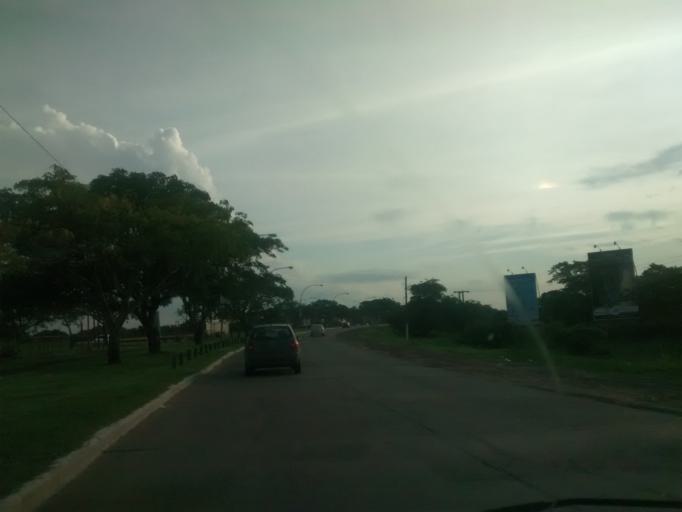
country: AR
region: Chaco
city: Resistencia
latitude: -27.4269
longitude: -58.9603
